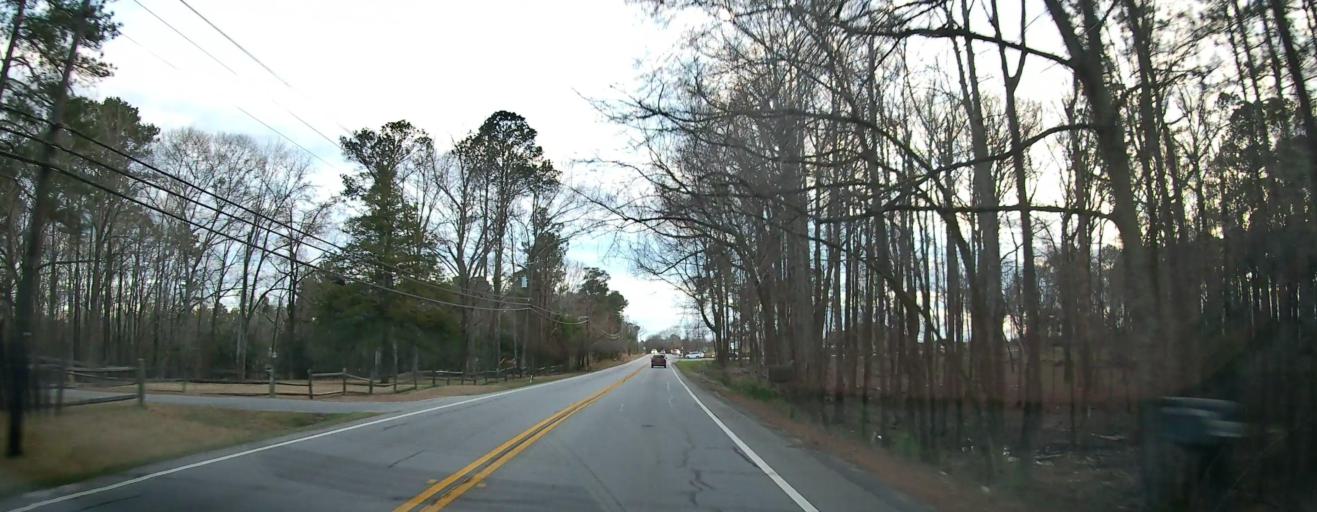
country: US
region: Alabama
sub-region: Russell County
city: Phenix City
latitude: 32.5910
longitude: -84.9094
